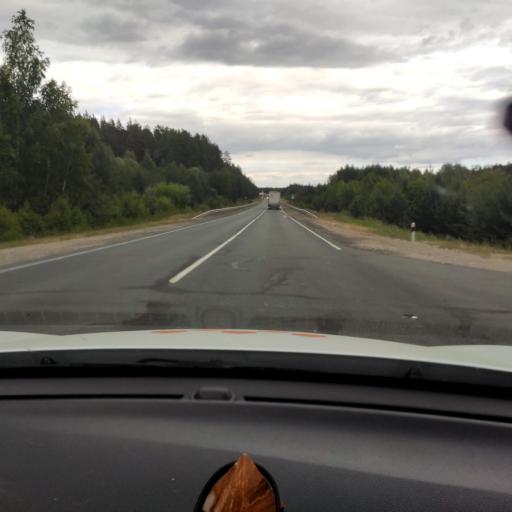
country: RU
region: Mariy-El
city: Volzhsk
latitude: 55.9003
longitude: 48.3863
